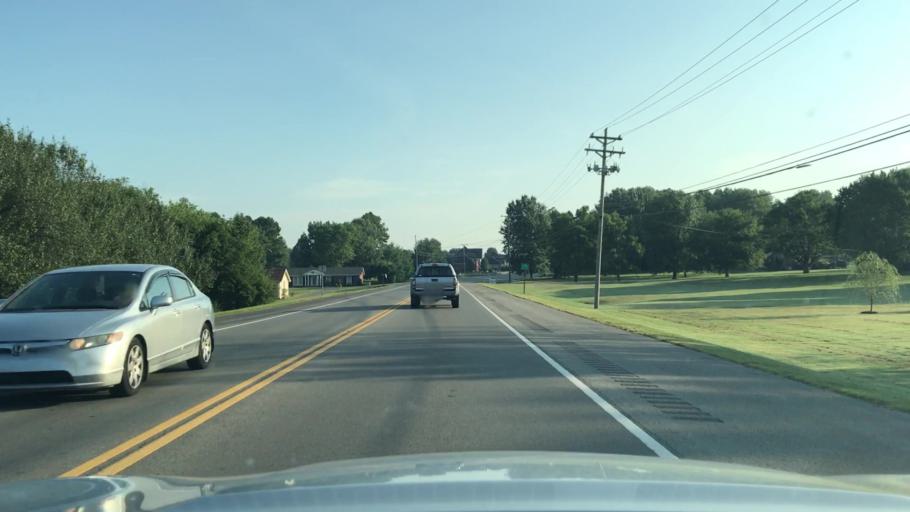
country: US
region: Tennessee
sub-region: Wilson County
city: Rural Hill
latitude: 36.1367
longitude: -86.5189
